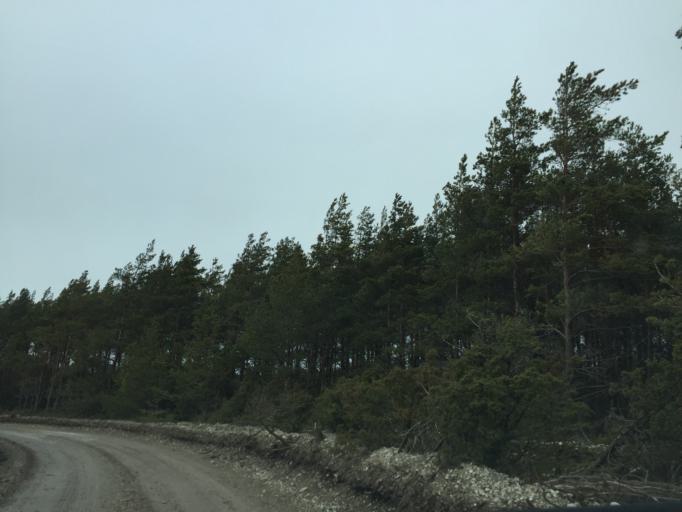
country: EE
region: Saare
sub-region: Kuressaare linn
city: Kuressaare
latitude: 58.5012
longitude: 21.9187
